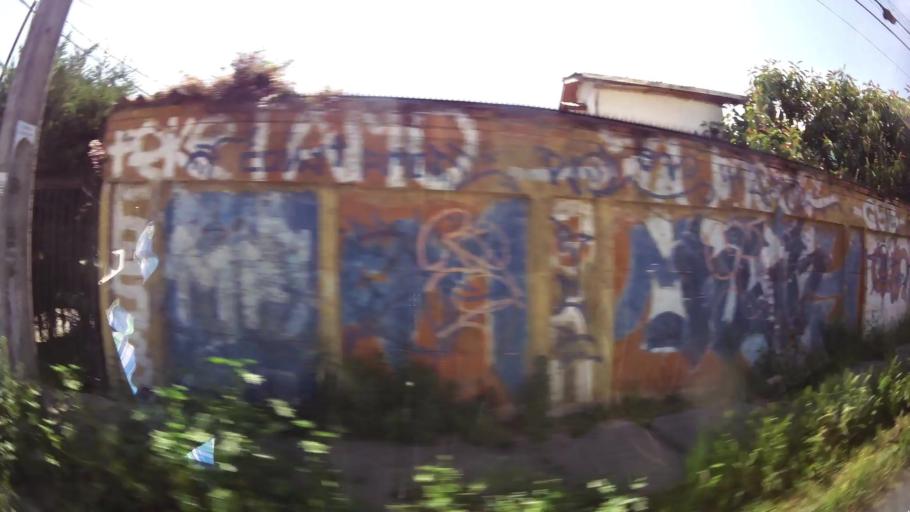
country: CL
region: Santiago Metropolitan
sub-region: Provincia de Santiago
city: Lo Prado
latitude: -33.4878
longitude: -70.7333
